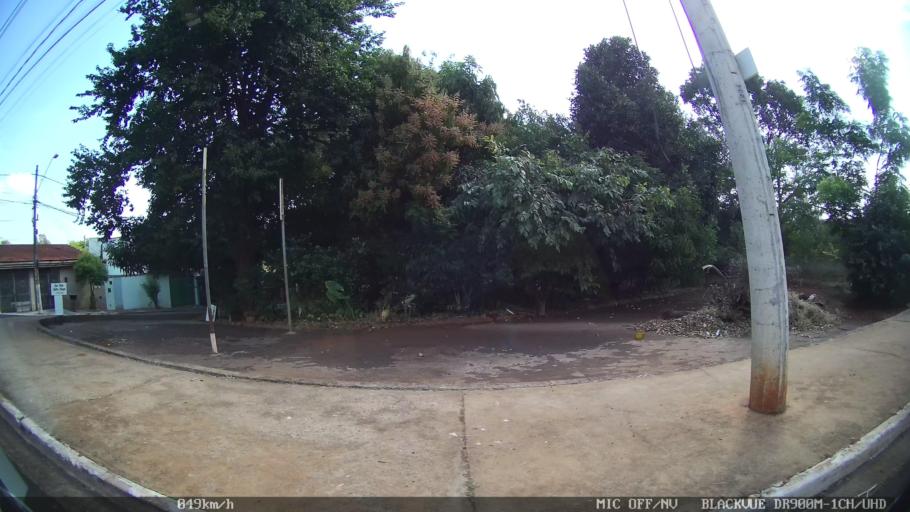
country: BR
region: Sao Paulo
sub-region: Ribeirao Preto
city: Ribeirao Preto
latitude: -21.1848
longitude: -47.8426
